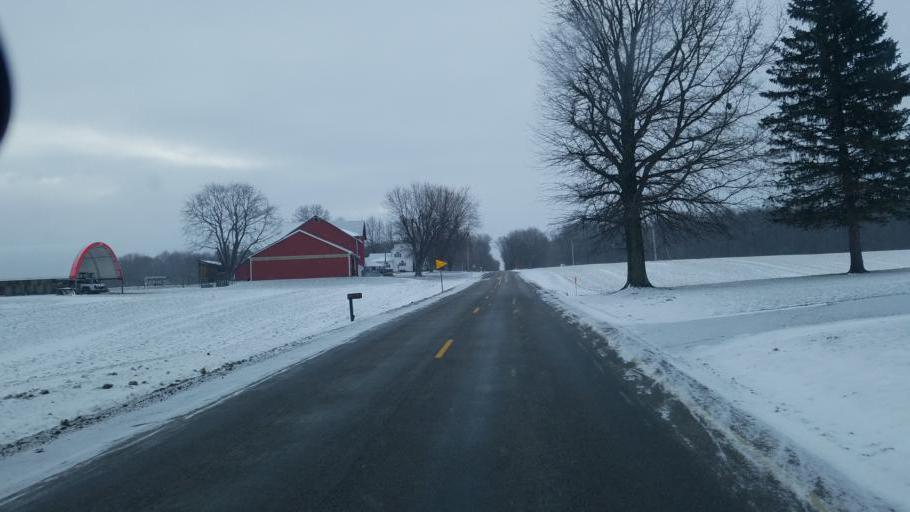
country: US
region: Pennsylvania
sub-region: Mercer County
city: Stoneboro
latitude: 41.4089
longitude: -80.0608
